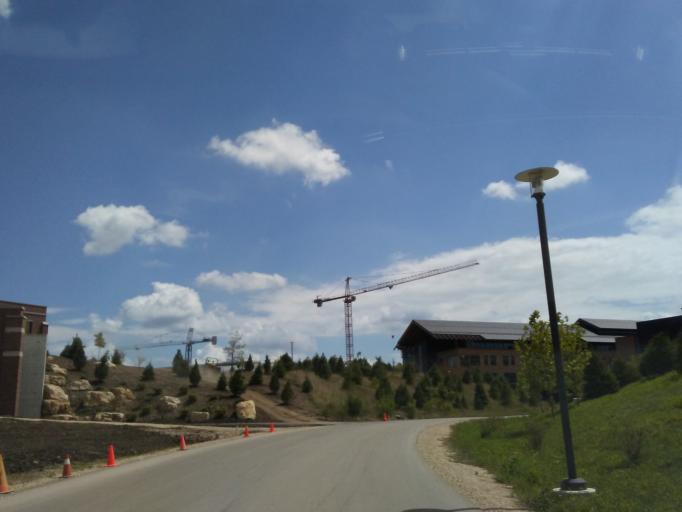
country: US
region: Wisconsin
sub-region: Dane County
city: Verona
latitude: 43.0000
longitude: -89.5664
